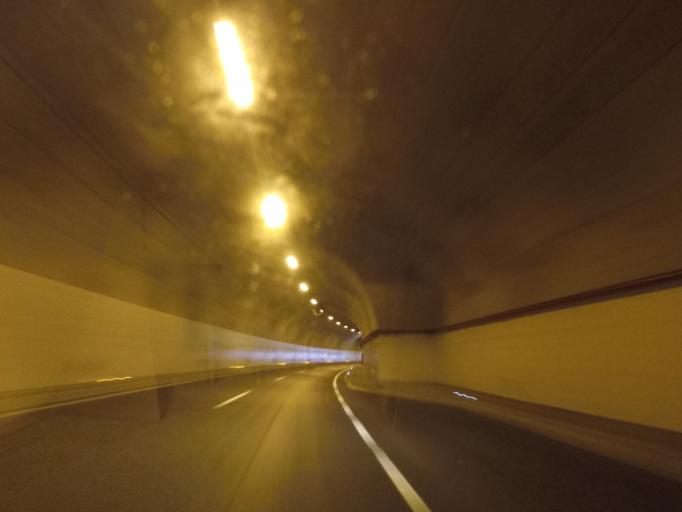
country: PT
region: Madeira
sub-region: Machico
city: Canical
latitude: 32.7443
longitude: -16.7402
